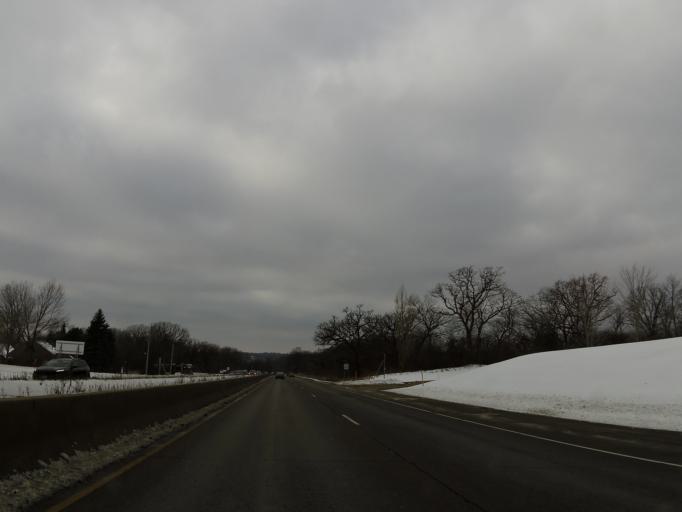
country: US
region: Minnesota
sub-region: Hennepin County
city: Minnetonka
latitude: 44.9194
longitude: -93.4848
